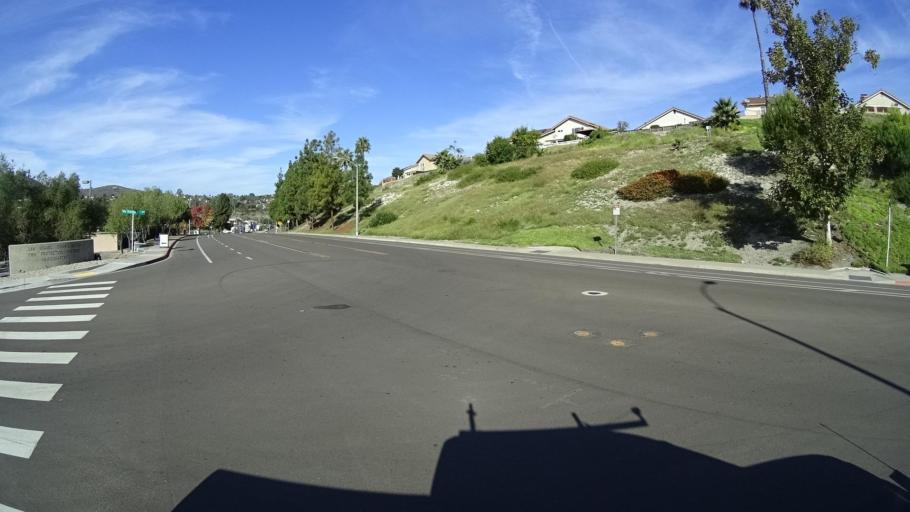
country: US
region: California
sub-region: San Diego County
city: Spring Valley
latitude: 32.7307
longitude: -116.9690
